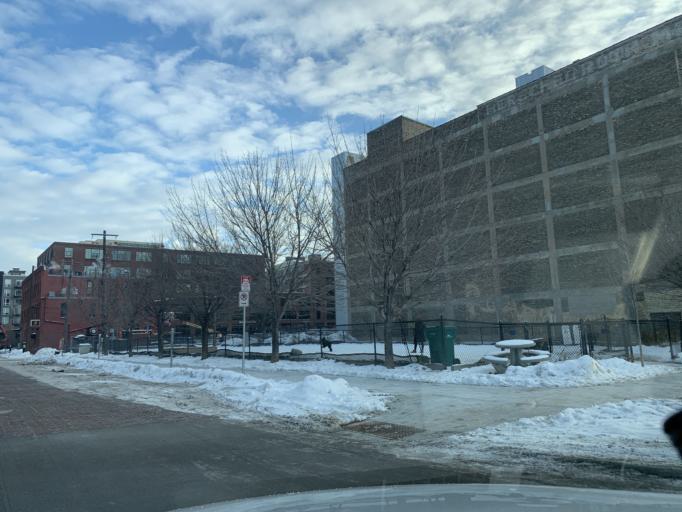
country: US
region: Minnesota
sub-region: Hennepin County
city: Minneapolis
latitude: 44.9881
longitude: -93.2798
